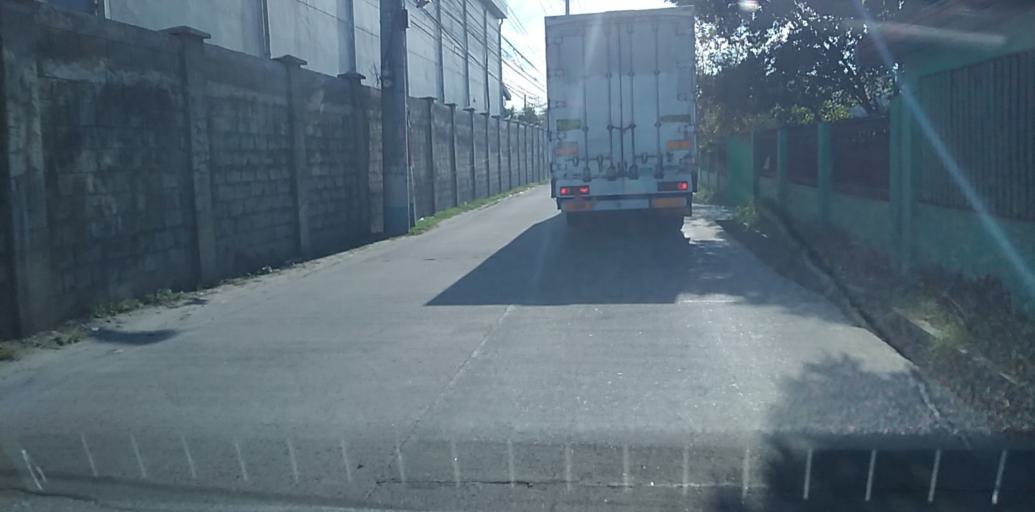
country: PH
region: Central Luzon
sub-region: Province of Pampanga
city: Telabastagan
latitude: 15.1054
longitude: 120.6243
